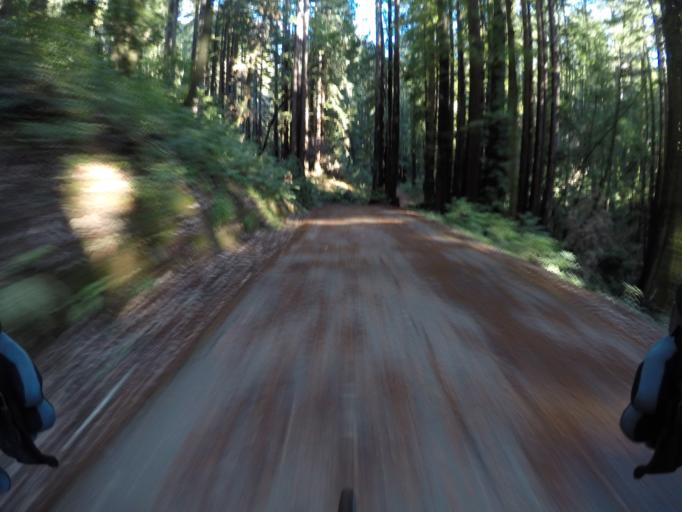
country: US
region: California
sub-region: Santa Cruz County
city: Mount Hermon
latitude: 37.0302
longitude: -122.0539
